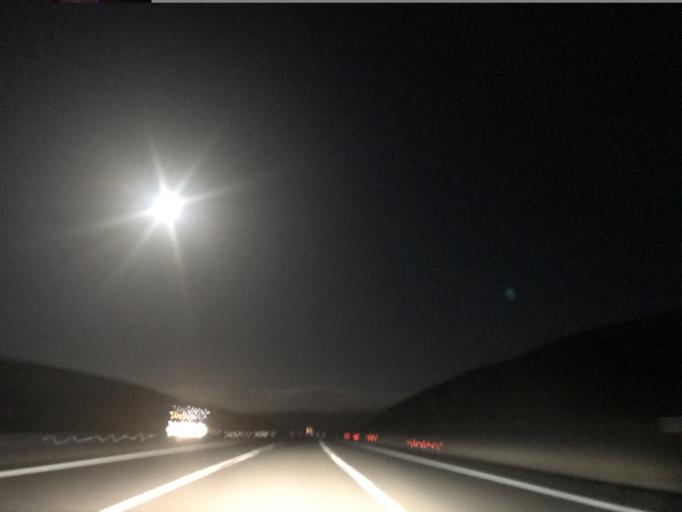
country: TR
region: Nigde
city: Ulukisla
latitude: 37.6351
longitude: 34.4436
